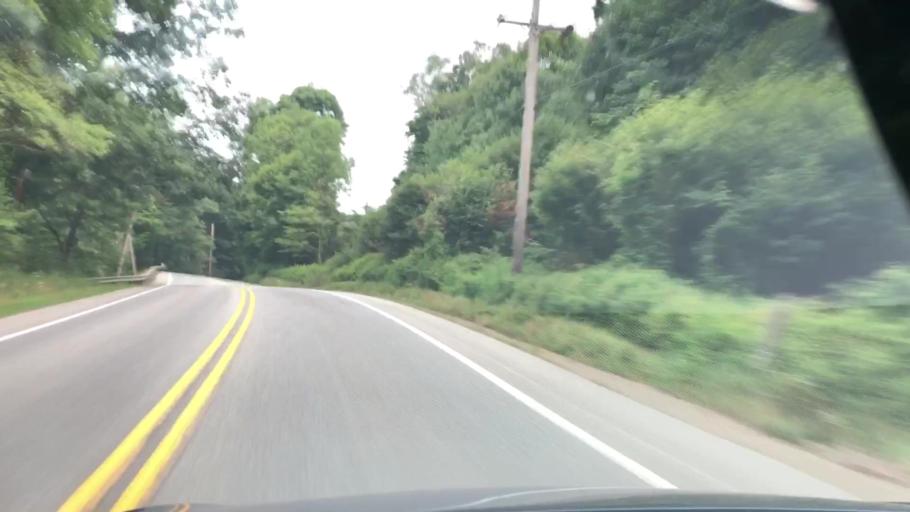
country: US
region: Pennsylvania
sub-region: Venango County
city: Hasson Heights
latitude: 41.5138
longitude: -79.7042
